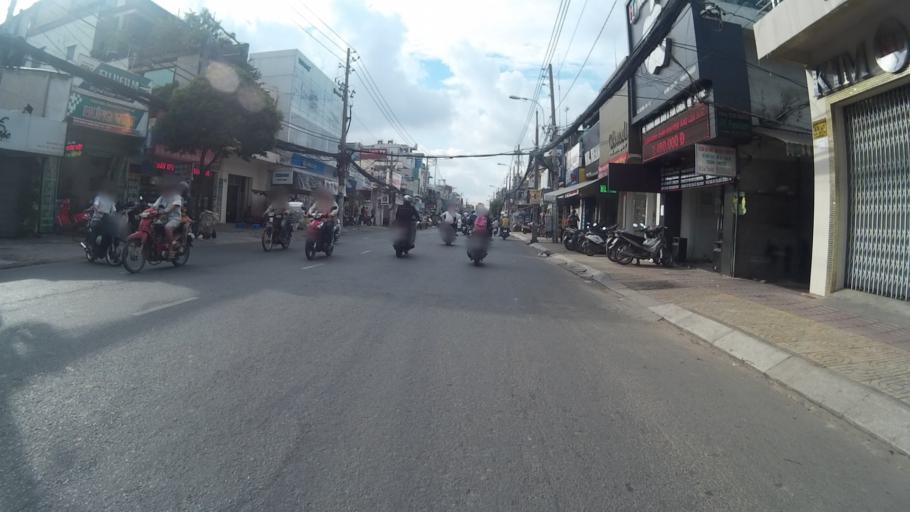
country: VN
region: Ho Chi Minh City
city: Quan Ba
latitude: 10.7813
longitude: 106.6752
